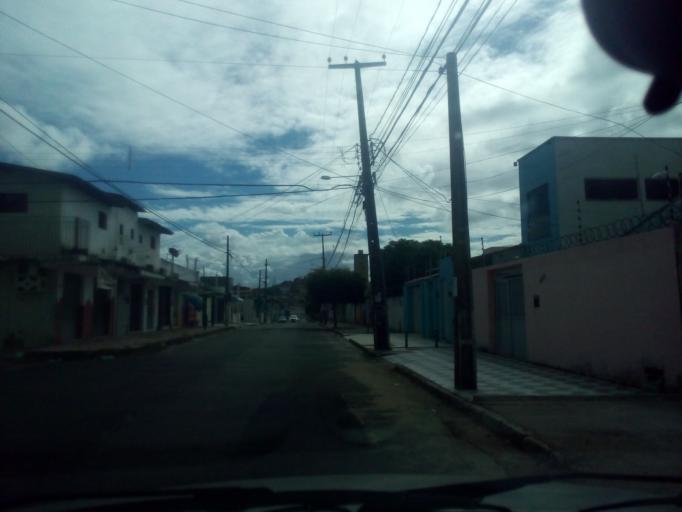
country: BR
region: Rio Grande do Norte
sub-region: Parnamirim
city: Parnamirim
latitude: -5.8703
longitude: -35.2049
